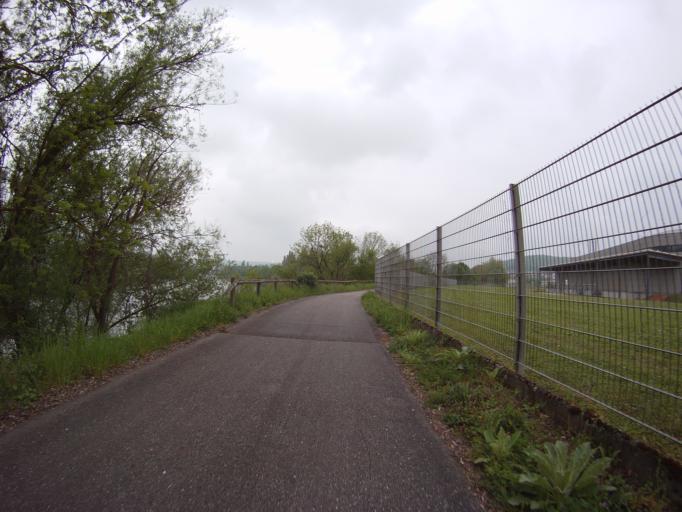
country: FR
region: Lorraine
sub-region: Departement de Meurthe-et-Moselle
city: Custines
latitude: 48.7813
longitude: 6.1414
